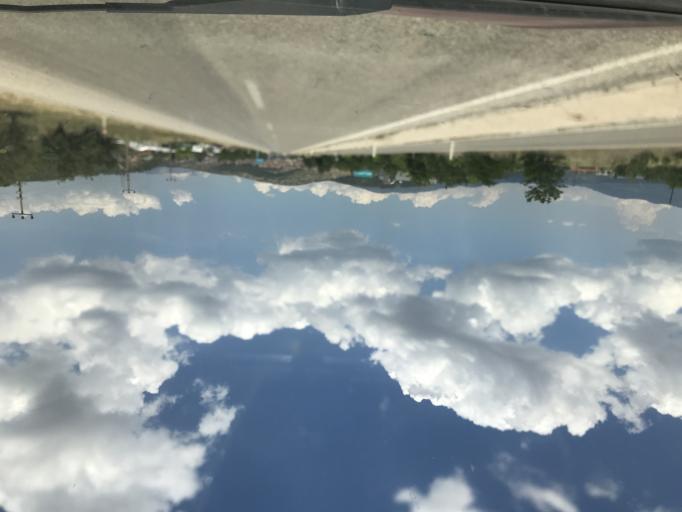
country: TR
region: Denizli
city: Tavas
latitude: 37.5538
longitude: 29.0538
